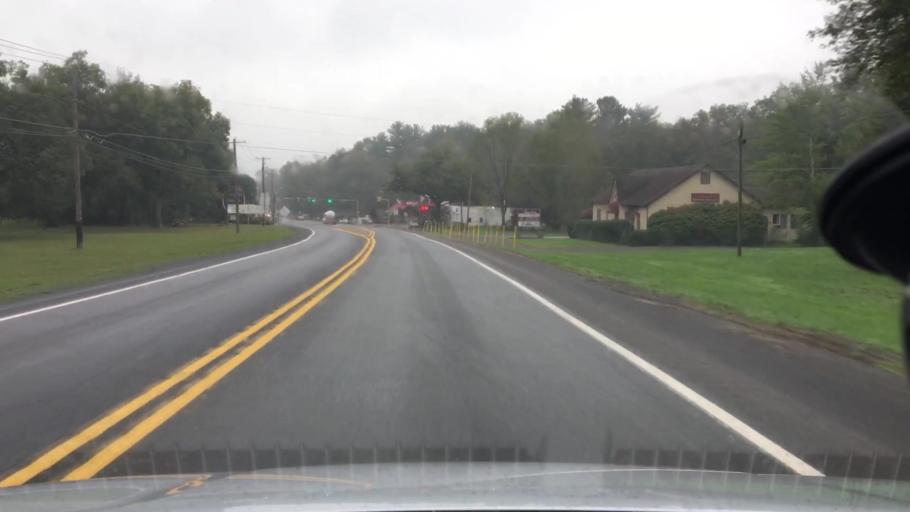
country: US
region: Pennsylvania
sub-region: Monroe County
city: Mount Pocono
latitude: 41.1278
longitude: -75.3126
